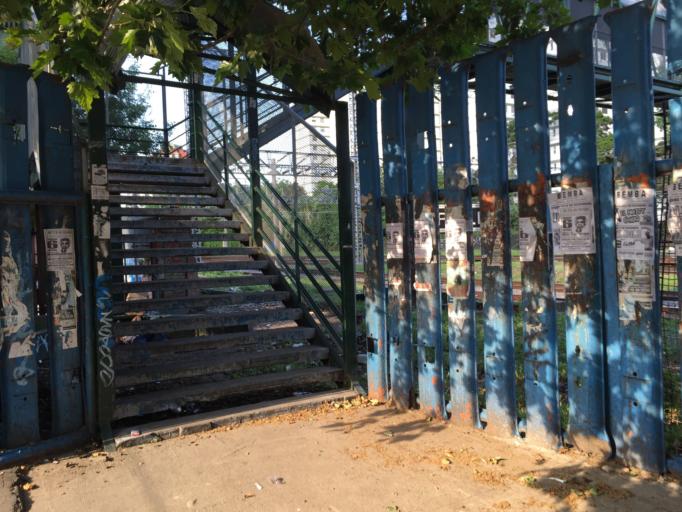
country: AR
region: Buenos Aires
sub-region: Partido de Lomas de Zamora
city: Lomas de Zamora
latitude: -34.7750
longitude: -58.3969
